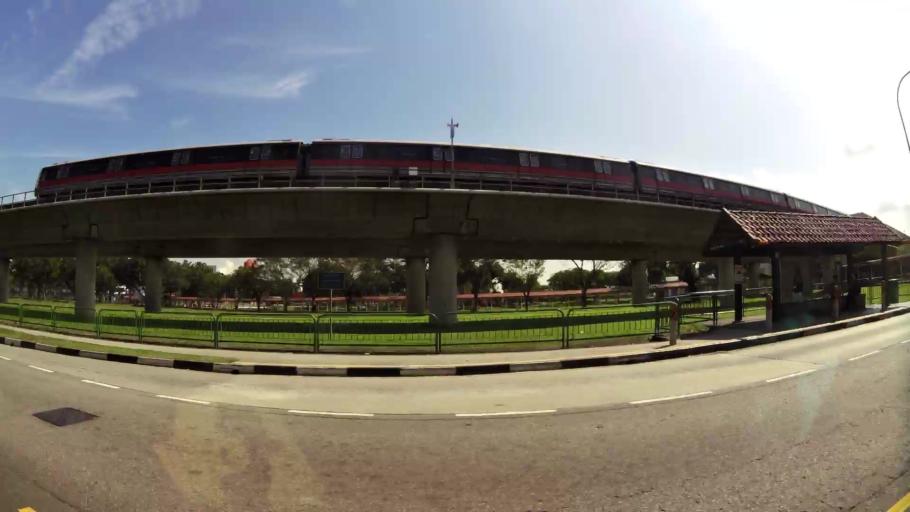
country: SG
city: Singapore
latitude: 1.3828
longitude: 103.8437
